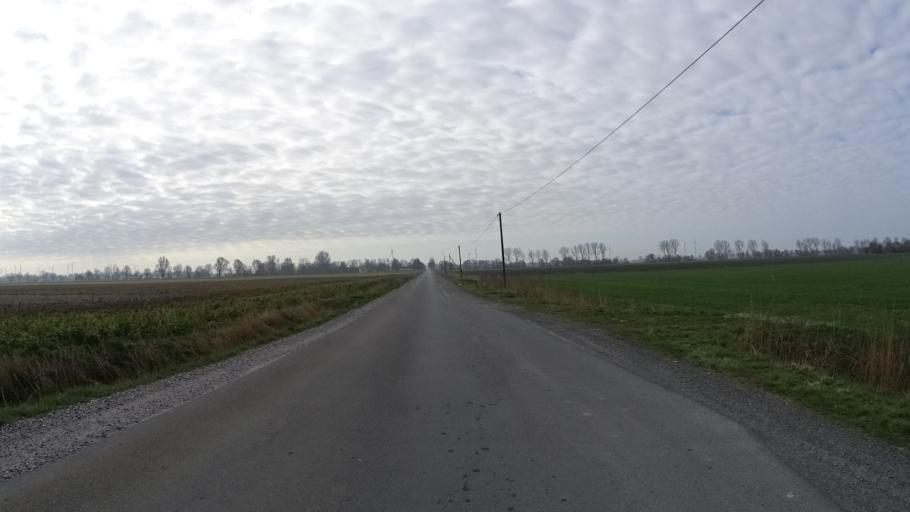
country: DE
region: Lower Saxony
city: Emden
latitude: 53.4018
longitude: 7.3246
